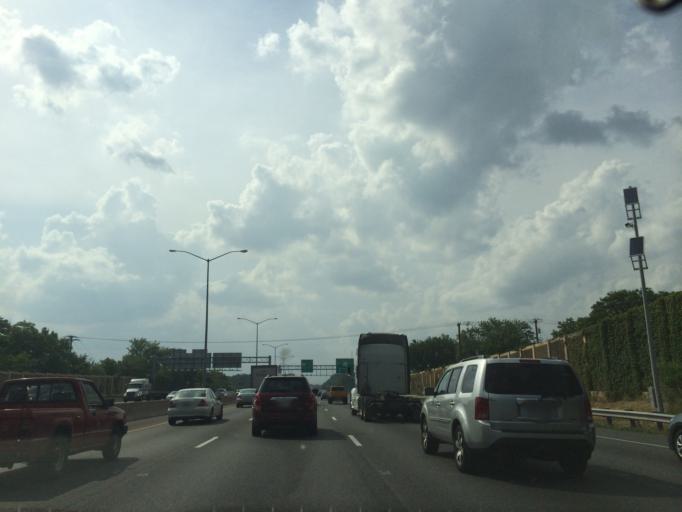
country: US
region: Maryland
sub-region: Baltimore County
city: Arbutus
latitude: 39.2594
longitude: -76.7010
